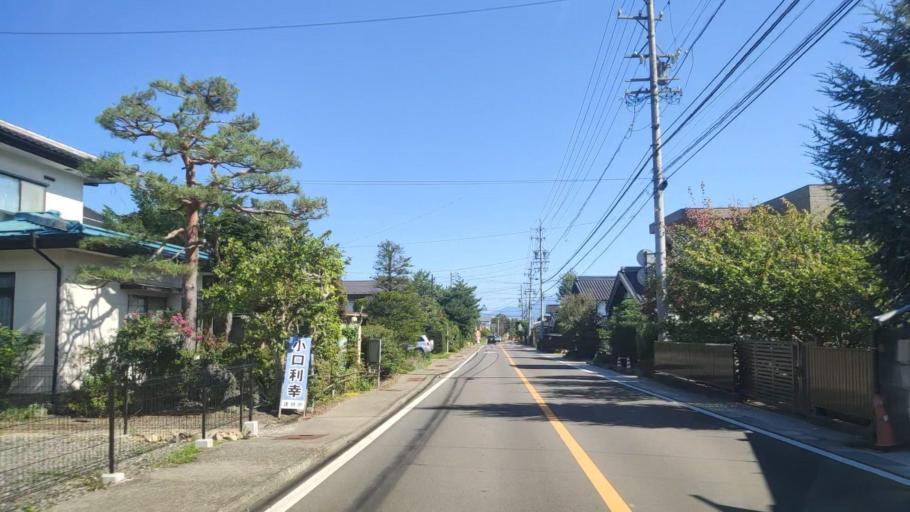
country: JP
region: Nagano
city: Shiojiri
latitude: 36.1373
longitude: 137.9382
